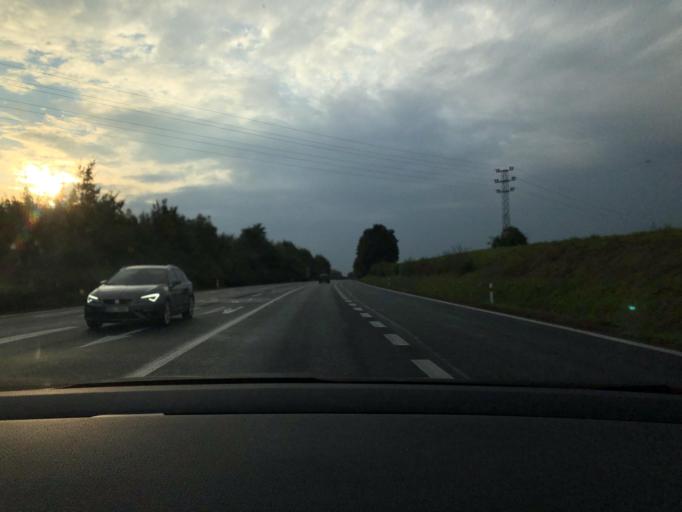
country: CZ
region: Central Bohemia
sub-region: Okres Kolin
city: Kolin
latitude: 50.0332
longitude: 15.1660
